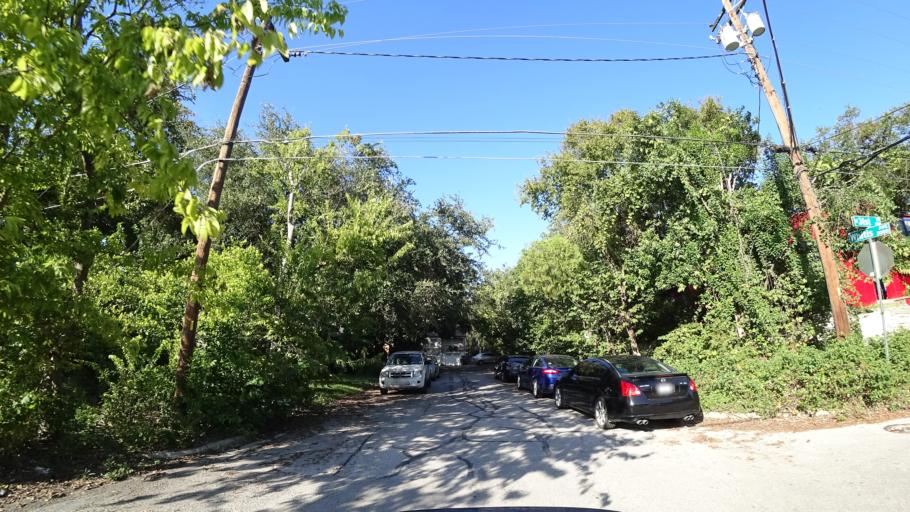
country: US
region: Texas
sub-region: Travis County
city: Austin
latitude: 30.2961
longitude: -97.7388
